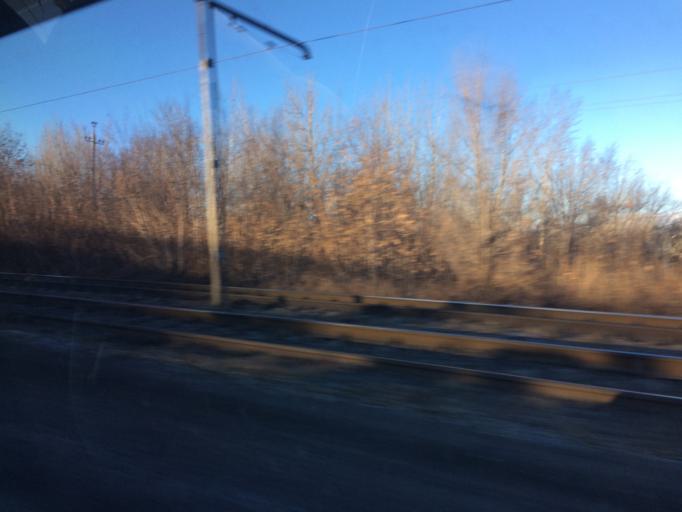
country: RU
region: Chelyabinsk
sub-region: Gorod Magnitogorsk
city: Magnitogorsk
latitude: 53.4077
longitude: 59.0303
